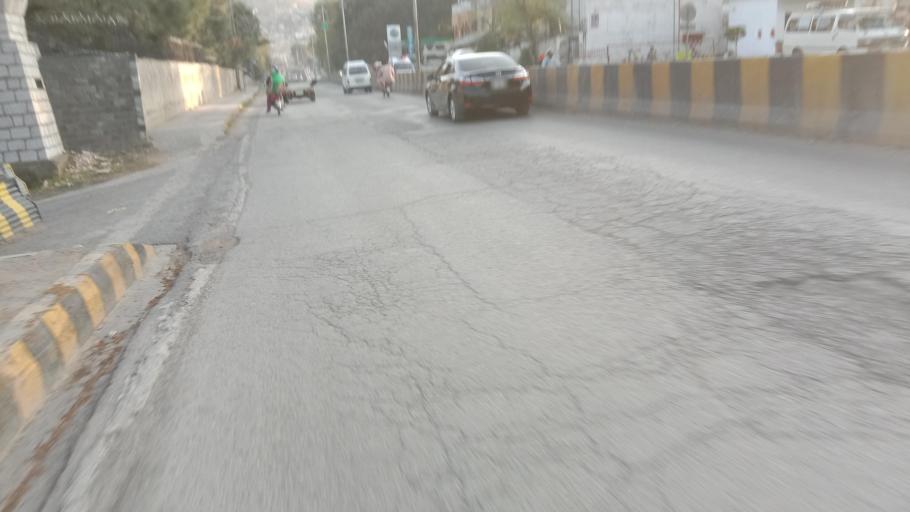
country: PK
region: Khyber Pakhtunkhwa
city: Abbottabad
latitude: 34.1518
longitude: 73.2174
